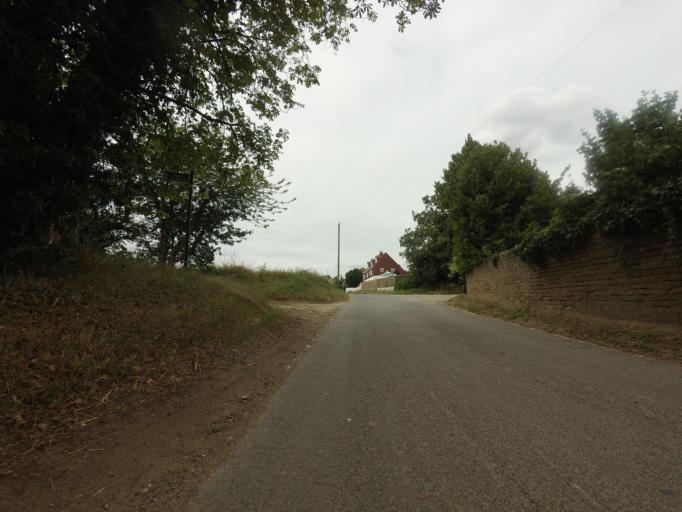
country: GB
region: England
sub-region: Medway
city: Stoke
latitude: 51.4378
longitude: 0.6059
